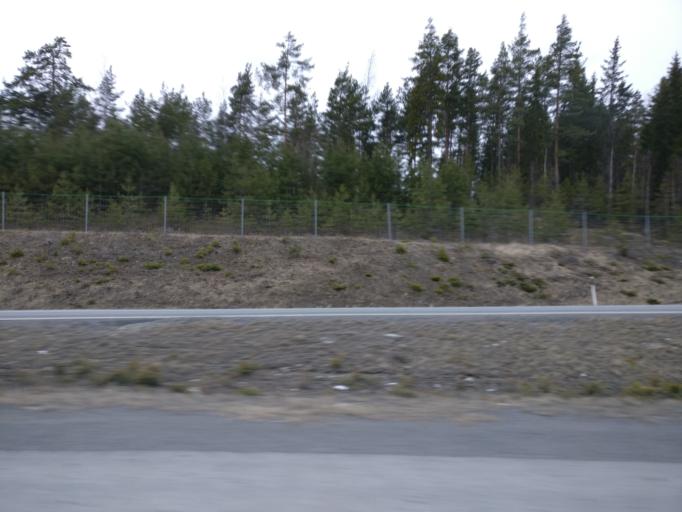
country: FI
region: Pirkanmaa
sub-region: Tampere
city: Lempaeaelae
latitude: 61.2911
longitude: 23.8133
